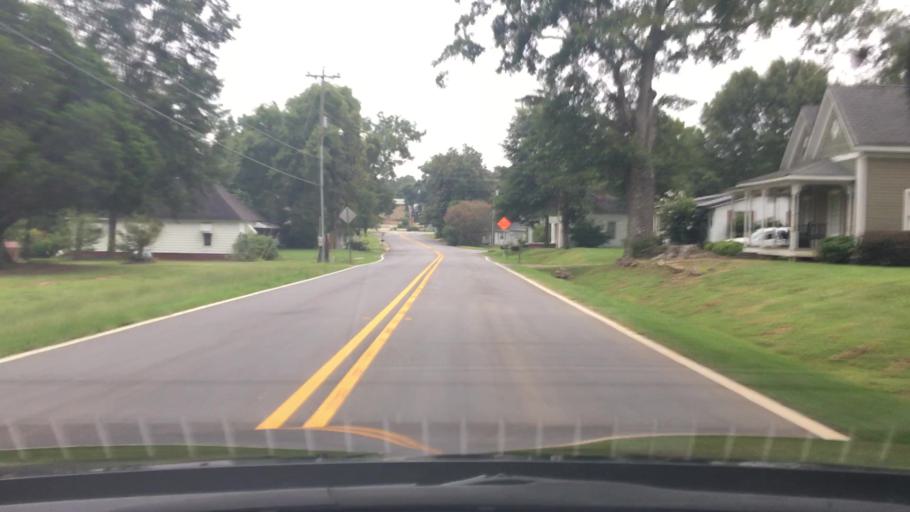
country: US
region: Georgia
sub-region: Coweta County
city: Senoia
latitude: 33.2926
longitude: -84.4596
